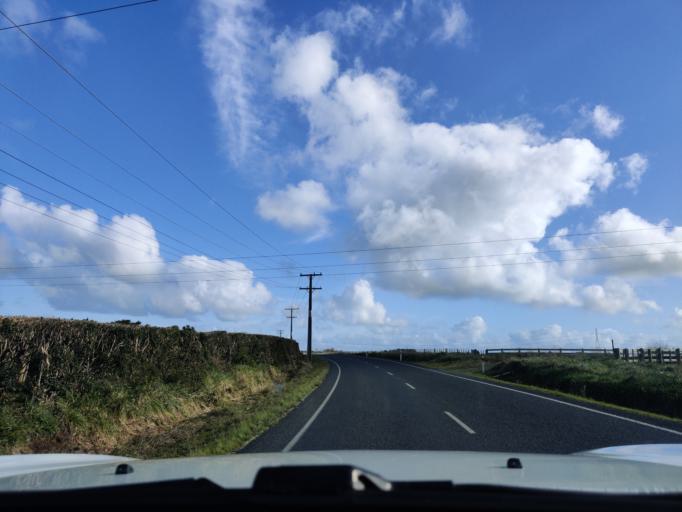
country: NZ
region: Waikato
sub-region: Waikato District
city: Te Kauwhata
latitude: -37.3604
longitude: 175.2546
